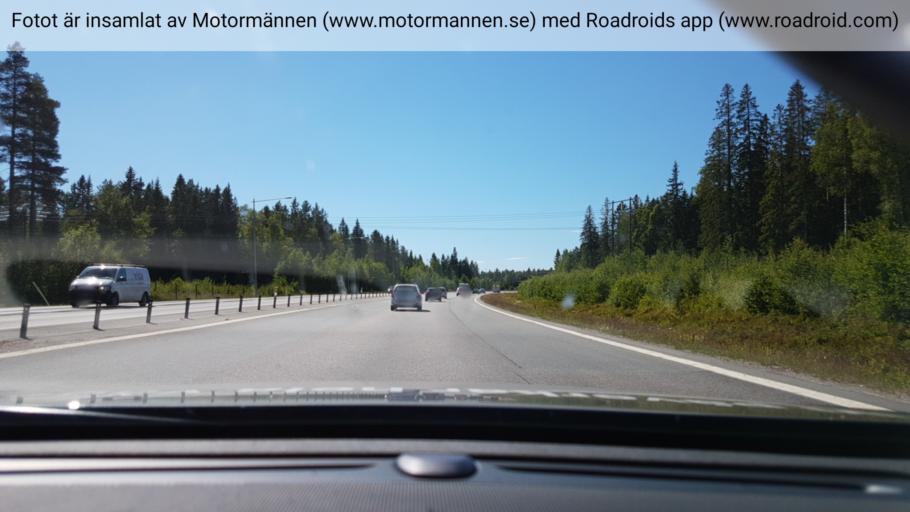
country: SE
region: Vaesterbotten
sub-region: Skelleftea Kommun
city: Skelleftea
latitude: 64.7648
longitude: 21.0129
